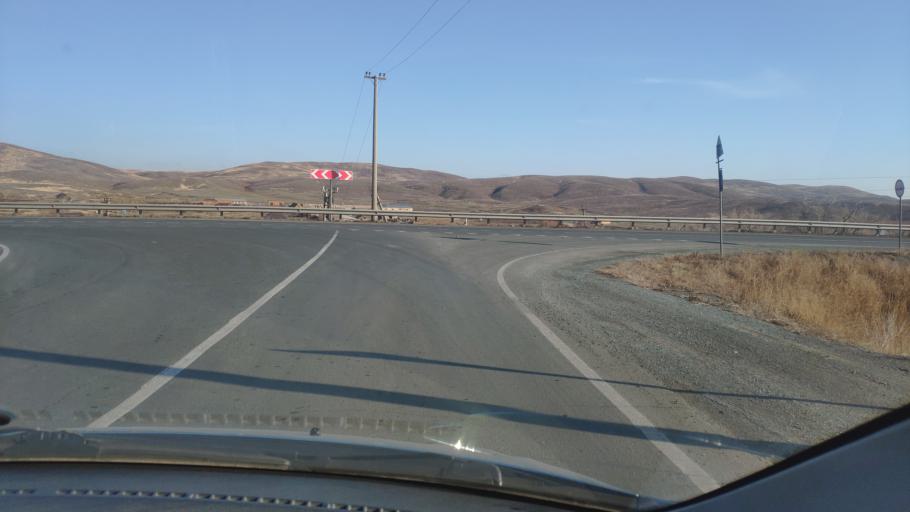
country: RU
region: Orenburg
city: Gay
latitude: 51.3437
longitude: 58.3963
